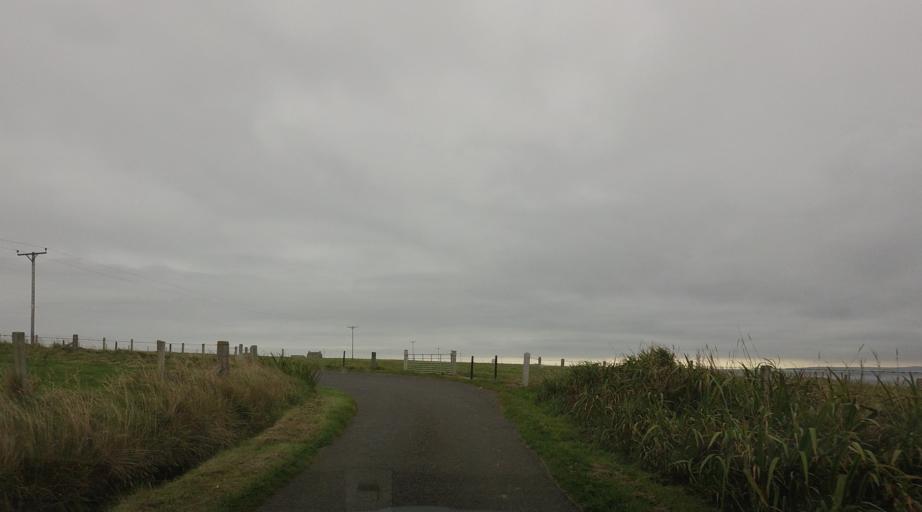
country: GB
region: Scotland
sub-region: Orkney Islands
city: Orkney
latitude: 58.7376
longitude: -2.9632
